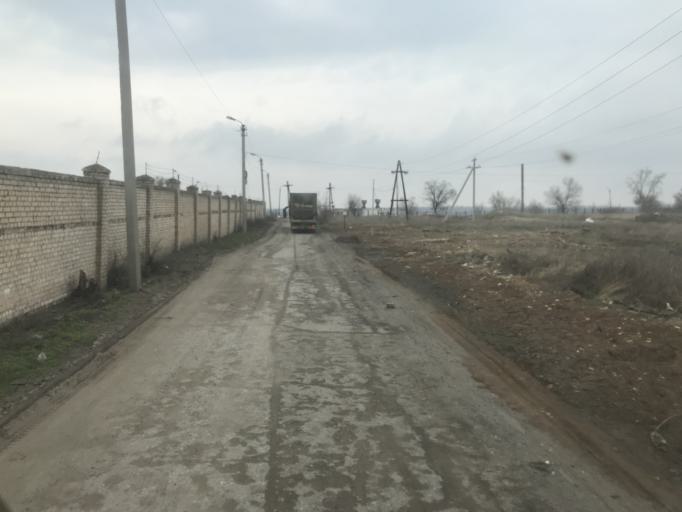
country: RU
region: Volgograd
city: Krasnoslobodsk
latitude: 48.5352
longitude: 44.5832
